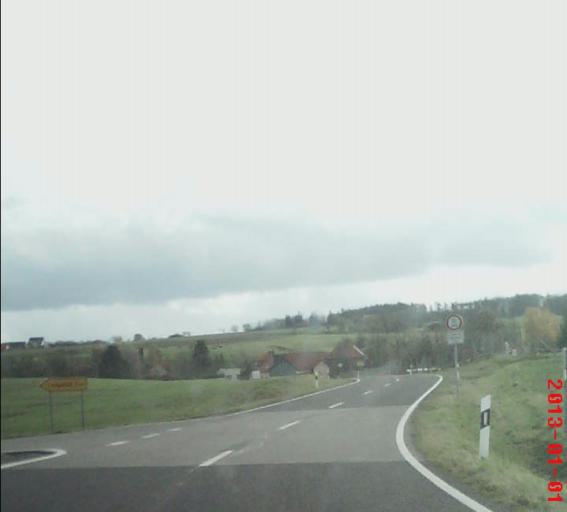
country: DE
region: Thuringia
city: Anrode
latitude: 51.2427
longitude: 10.3713
